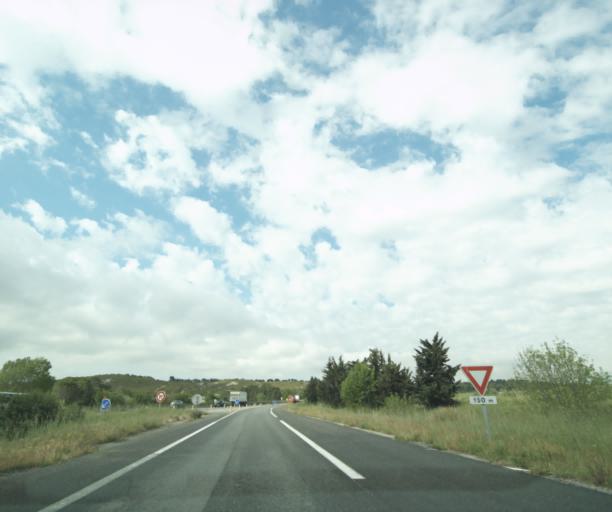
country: FR
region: Provence-Alpes-Cote d'Azur
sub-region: Departement des Bouches-du-Rhone
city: Cabries
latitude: 43.4781
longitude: 5.3533
